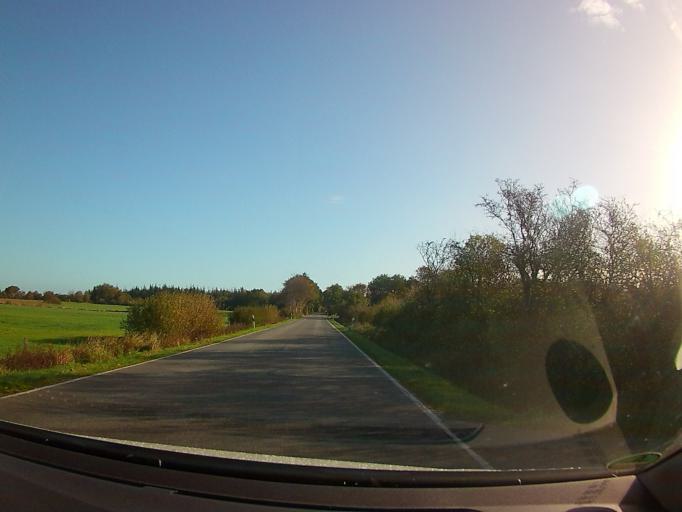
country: DE
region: Schleswig-Holstein
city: Drelsdorf
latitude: 54.6038
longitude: 9.0718
